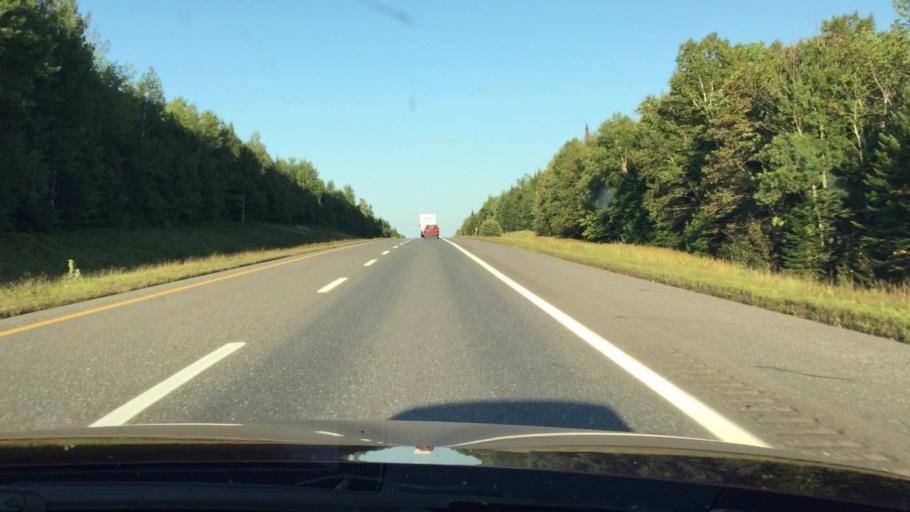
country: US
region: Maine
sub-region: Aroostook County
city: Hodgdon
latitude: 46.1399
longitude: -68.0087
